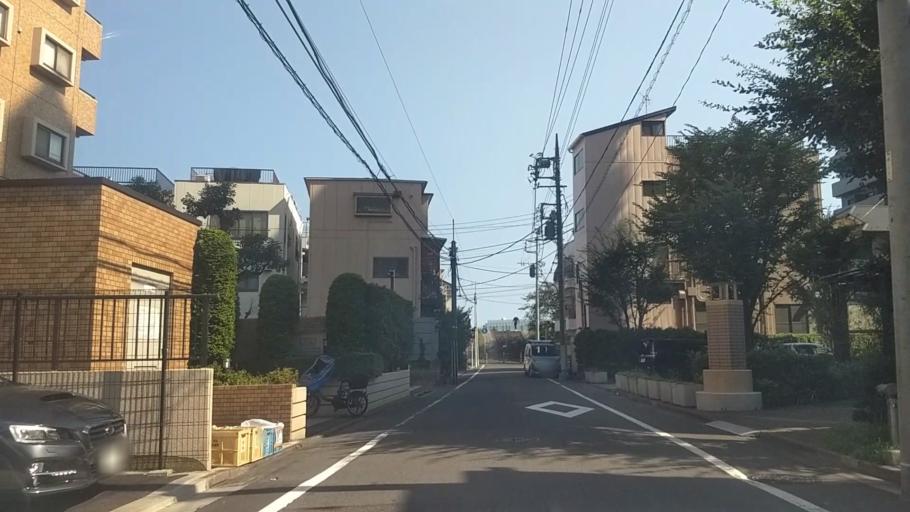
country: JP
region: Kanagawa
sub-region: Kawasaki-shi
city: Kawasaki
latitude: 35.5428
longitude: 139.7170
